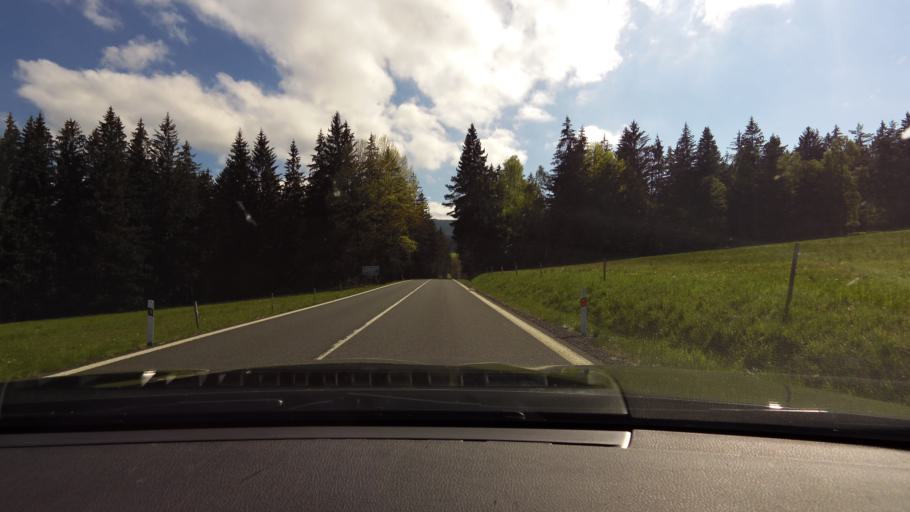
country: CZ
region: Plzensky
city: Strazov
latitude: 49.2388
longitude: 13.2915
